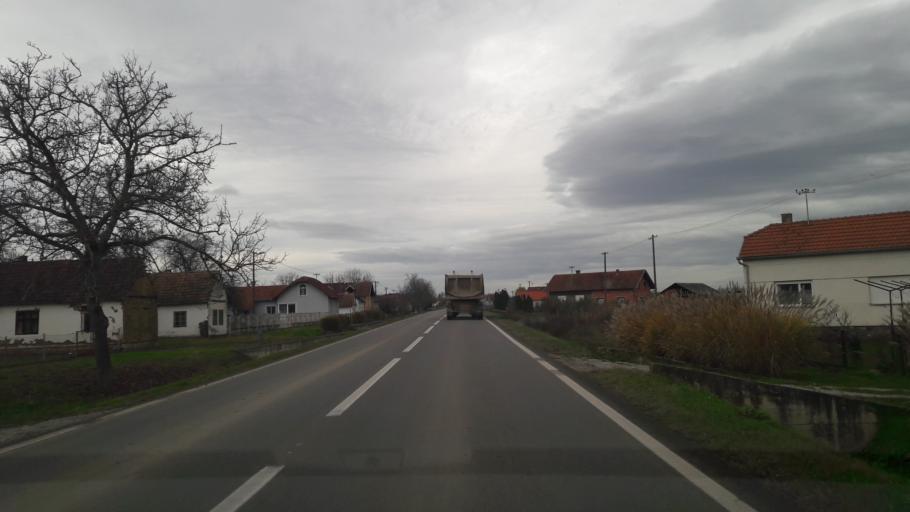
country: HR
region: Osjecko-Baranjska
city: Fericanci
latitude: 45.5257
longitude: 17.9637
